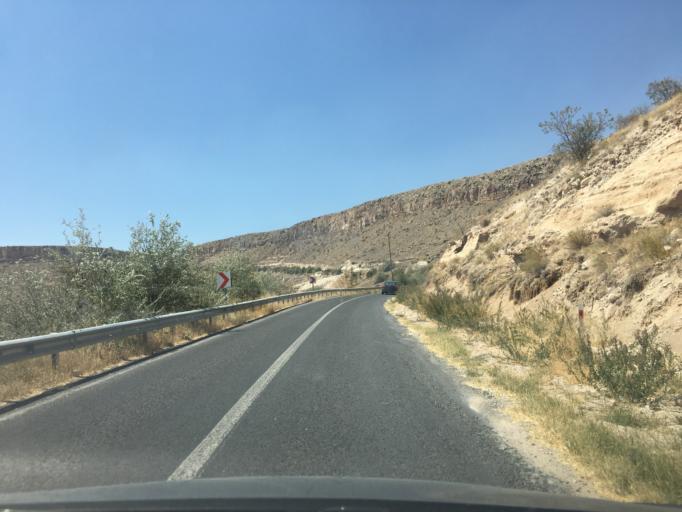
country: TR
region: Nevsehir
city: Urgub
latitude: 38.4698
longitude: 34.9451
